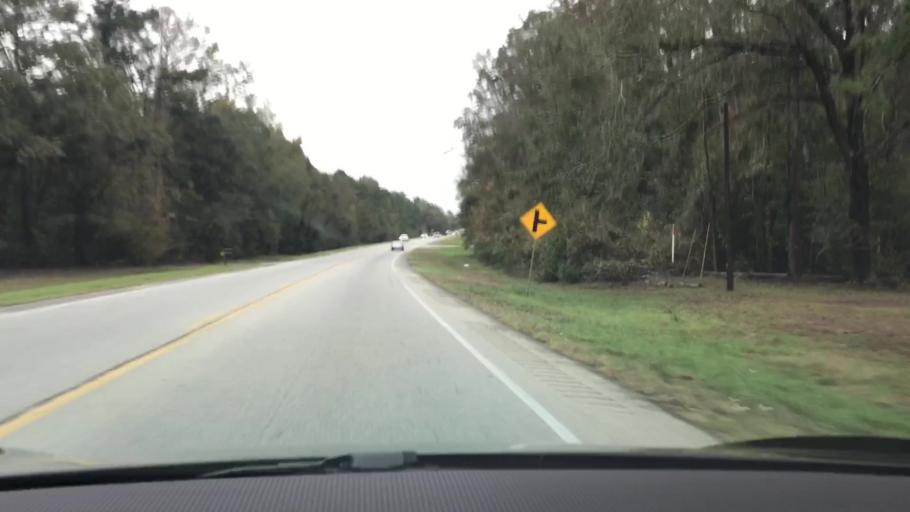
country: US
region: Georgia
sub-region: Jefferson County
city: Louisville
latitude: 32.9769
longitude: -82.3907
